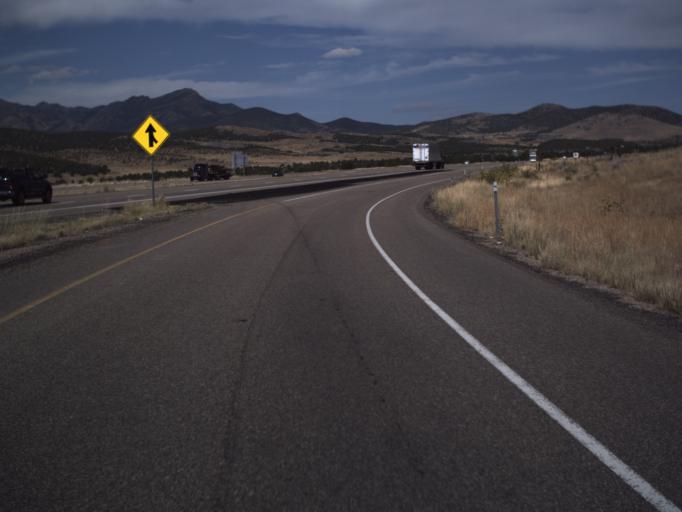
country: US
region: Utah
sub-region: Millard County
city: Fillmore
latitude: 39.1464
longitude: -112.2343
